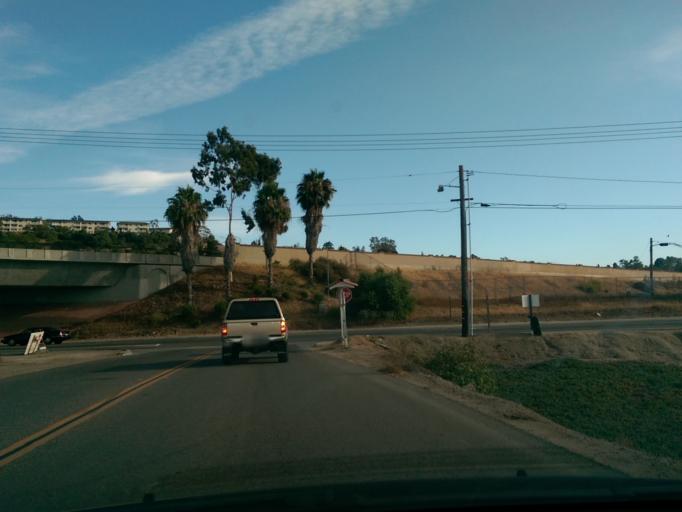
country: US
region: California
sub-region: San Diego County
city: Camp Pendleton South
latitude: 33.2307
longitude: -117.3139
